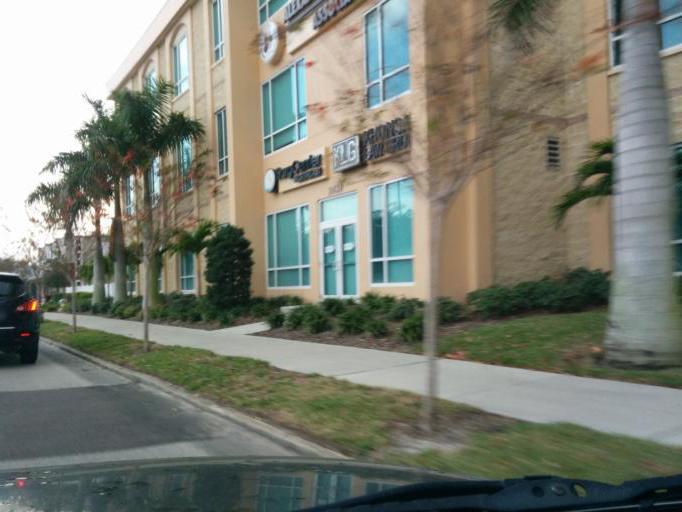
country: US
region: Florida
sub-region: Pinellas County
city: Saint Petersburg
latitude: 27.7947
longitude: -82.6468
